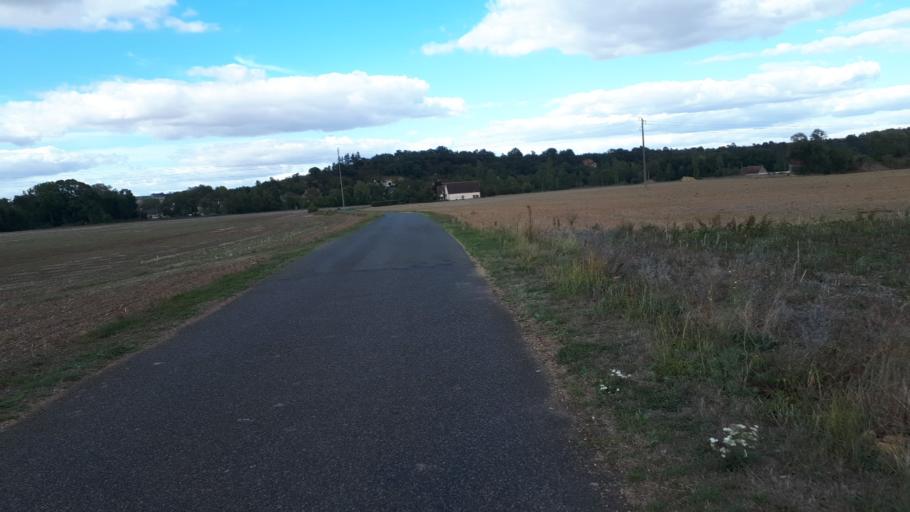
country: FR
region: Centre
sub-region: Departement du Loir-et-Cher
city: Villiers-sur-Loir
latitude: 47.8052
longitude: 0.9606
